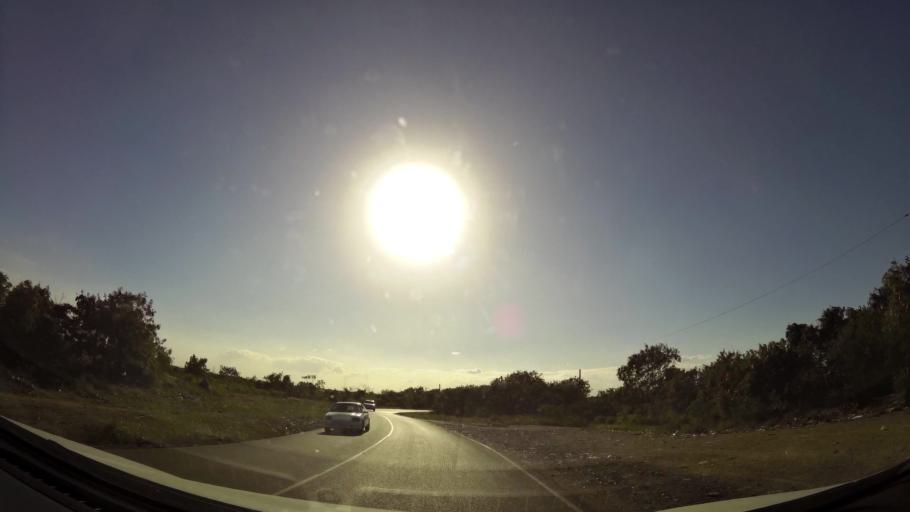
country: DO
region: Santo Domingo
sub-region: Santo Domingo
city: Santo Domingo Este
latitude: 18.4828
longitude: -69.8063
